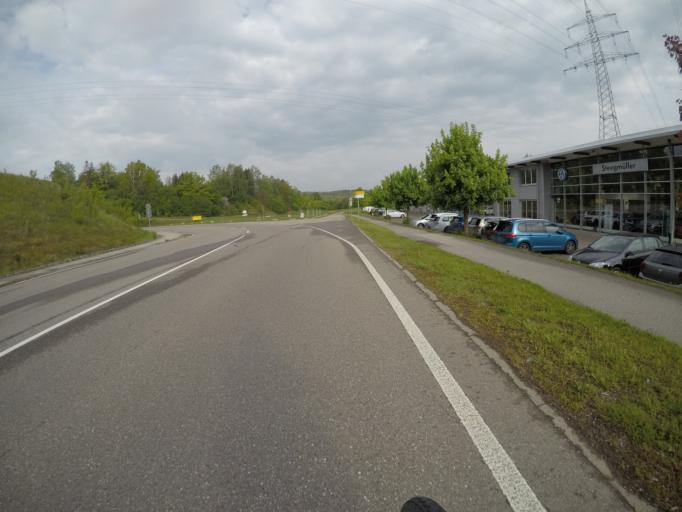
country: DE
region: Baden-Wuerttemberg
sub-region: Regierungsbezirk Stuttgart
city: Magstadt
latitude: 48.7465
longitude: 8.9521
